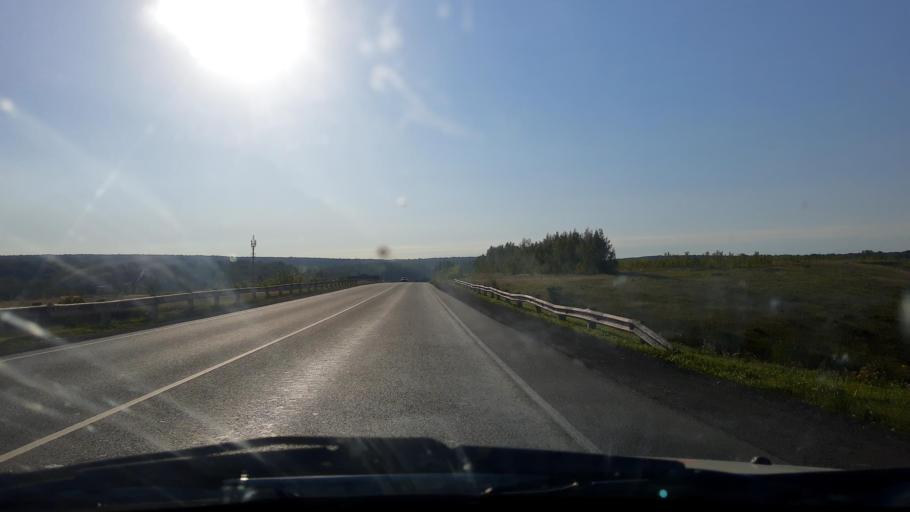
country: RU
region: Bashkortostan
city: Oktyabr'skiy
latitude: 54.4368
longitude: 53.4618
